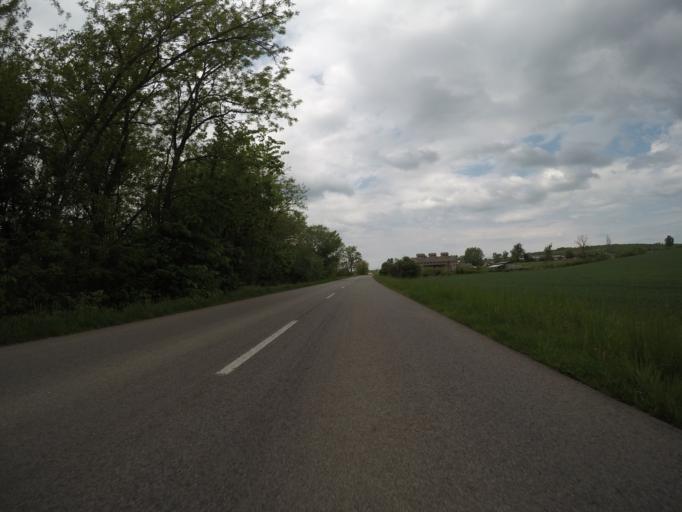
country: SK
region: Nitriansky
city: Sahy
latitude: 48.0654
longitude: 18.8506
